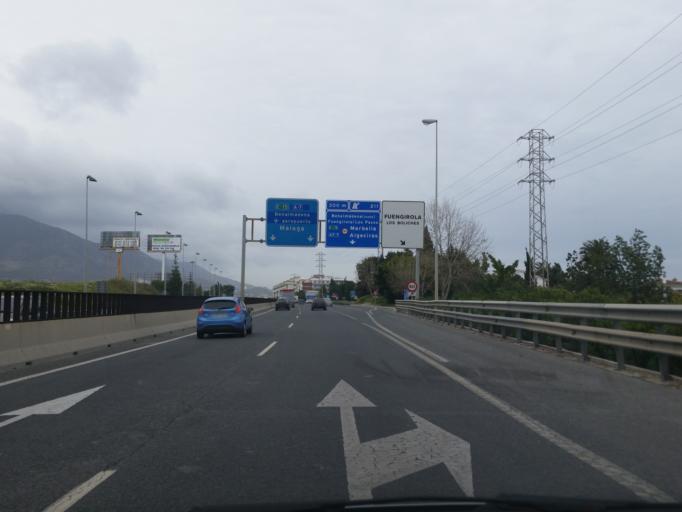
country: ES
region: Andalusia
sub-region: Provincia de Malaga
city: Fuengirola
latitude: 36.5524
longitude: -4.6247
